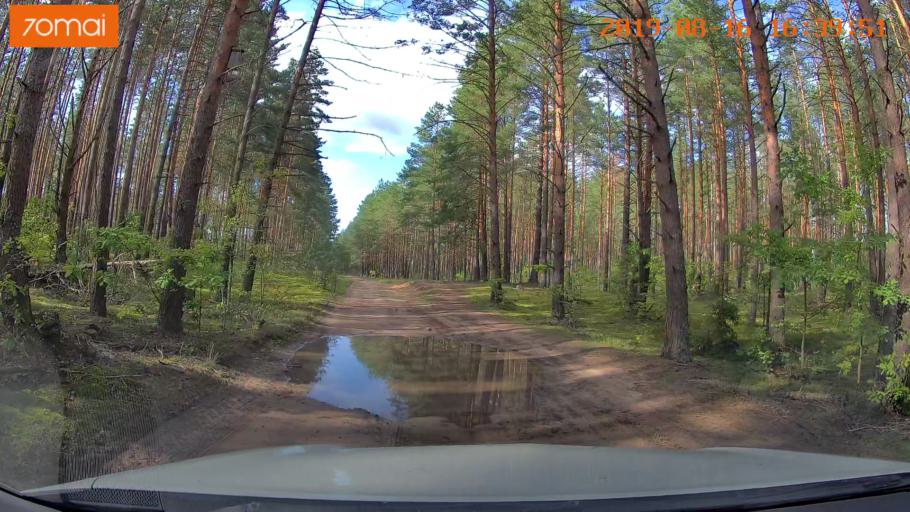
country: BY
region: Mogilev
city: Asipovichy
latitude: 53.2357
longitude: 28.7776
